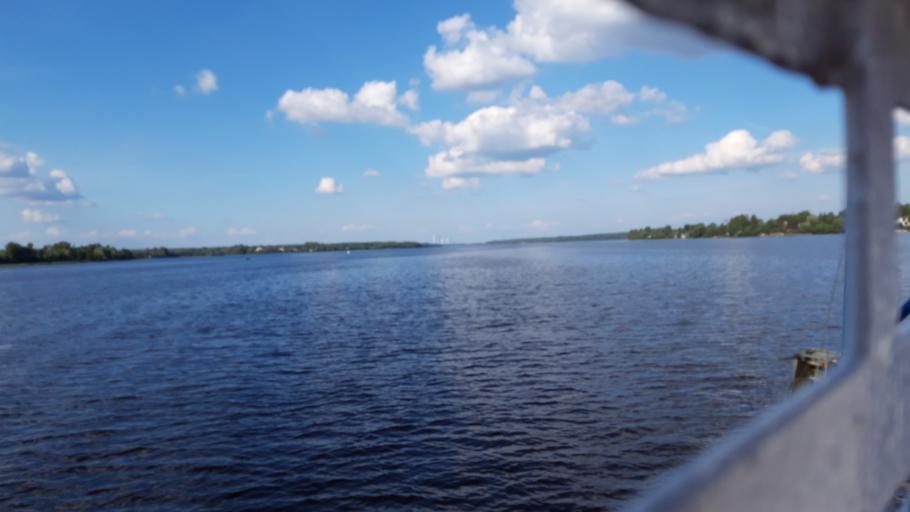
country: RU
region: Tverskaya
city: Konakovo
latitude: 56.6574
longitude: 36.6398
